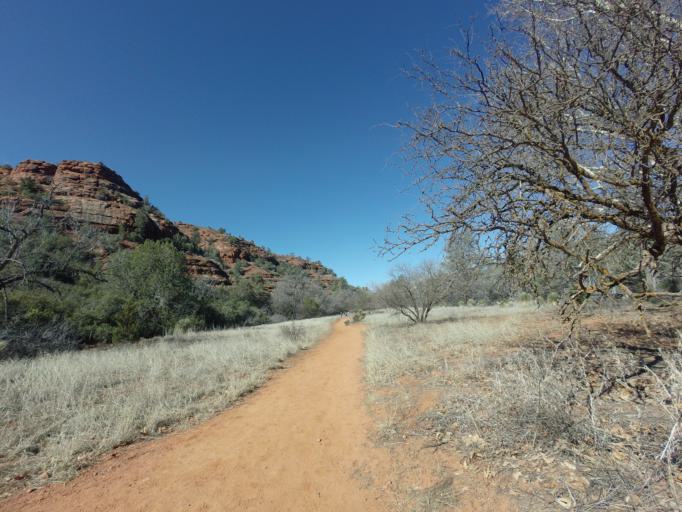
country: US
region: Arizona
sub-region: Yavapai County
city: West Sedona
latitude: 34.8225
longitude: -111.7998
